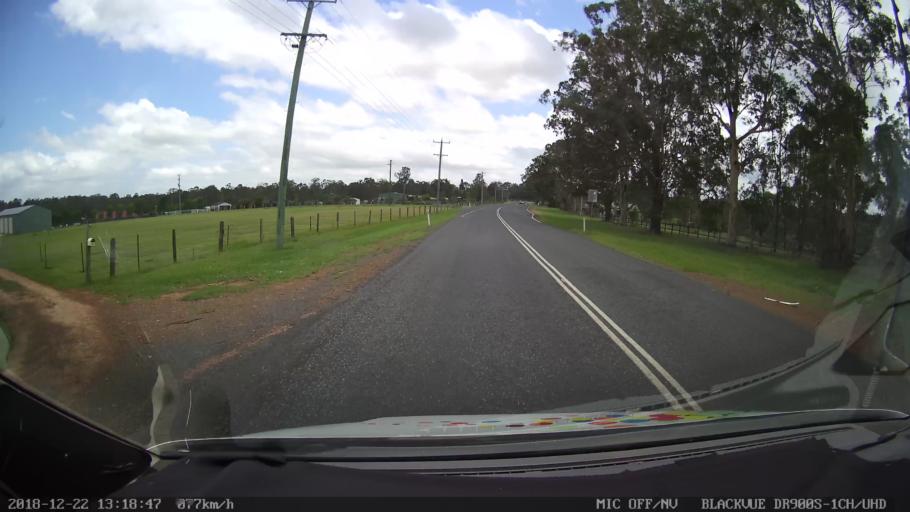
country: AU
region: New South Wales
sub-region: Clarence Valley
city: South Grafton
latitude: -29.7502
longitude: 152.9325
